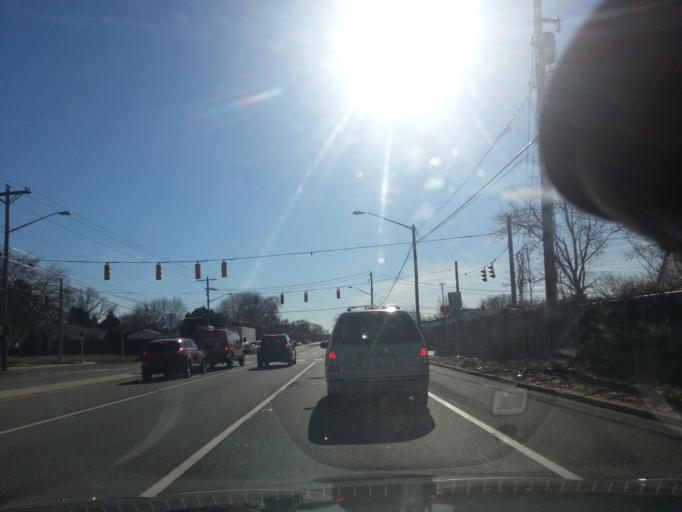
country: US
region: Delaware
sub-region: New Castle County
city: Brookside
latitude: 39.6773
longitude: -75.6869
